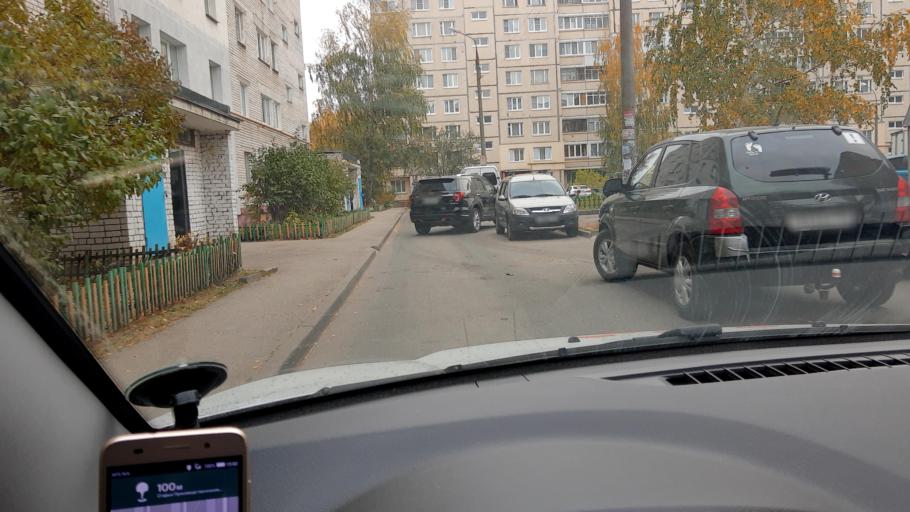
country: RU
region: Nizjnij Novgorod
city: Burevestnik
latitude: 56.2274
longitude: 43.8610
